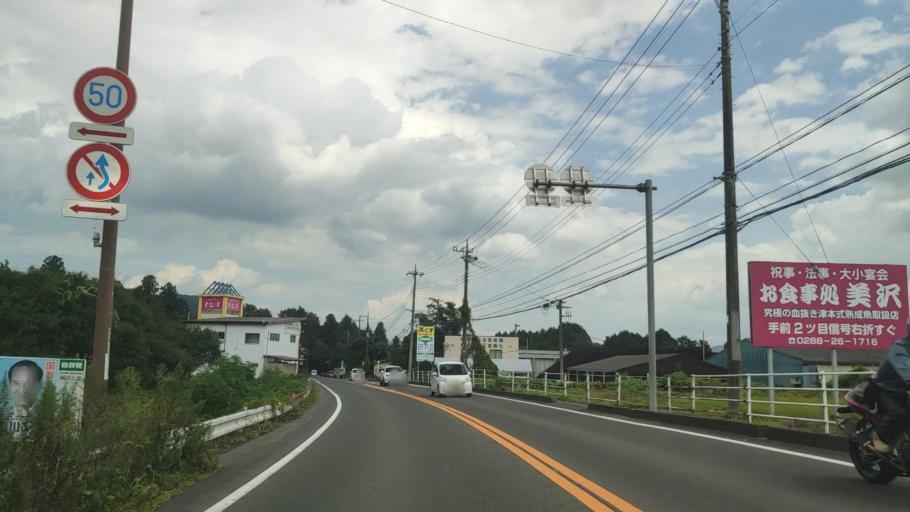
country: JP
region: Tochigi
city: Imaichi
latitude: 36.6903
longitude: 139.7635
